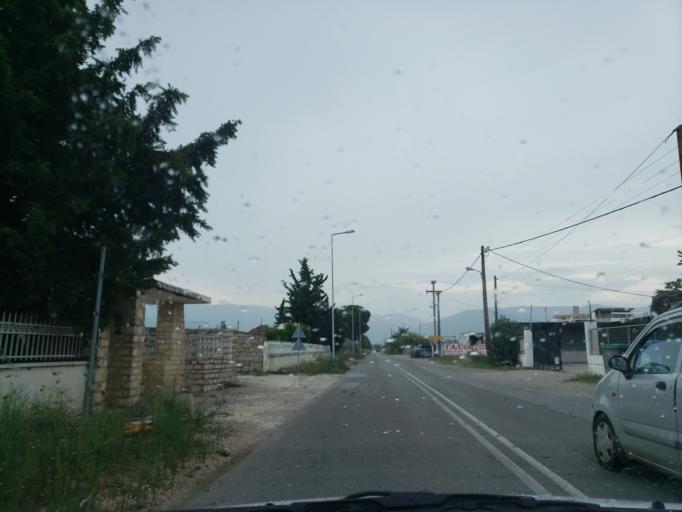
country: GR
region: Central Greece
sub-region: Nomos Fthiotidos
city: Rodhitsa
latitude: 38.8646
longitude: 22.4400
